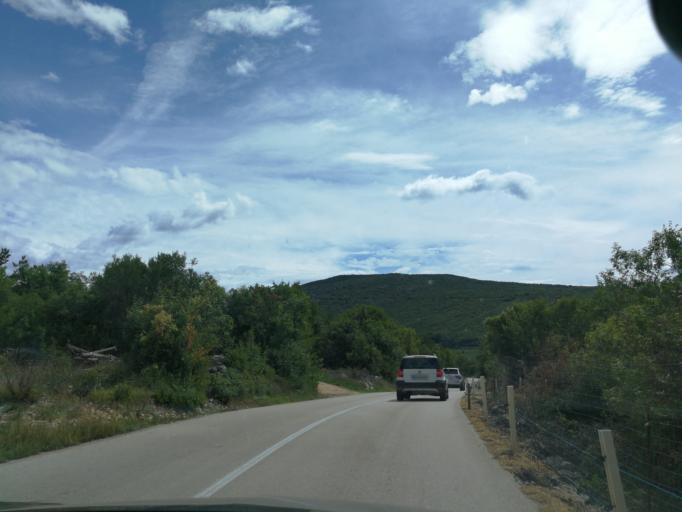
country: HR
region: Primorsko-Goranska
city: Punat
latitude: 45.0729
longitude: 14.6614
